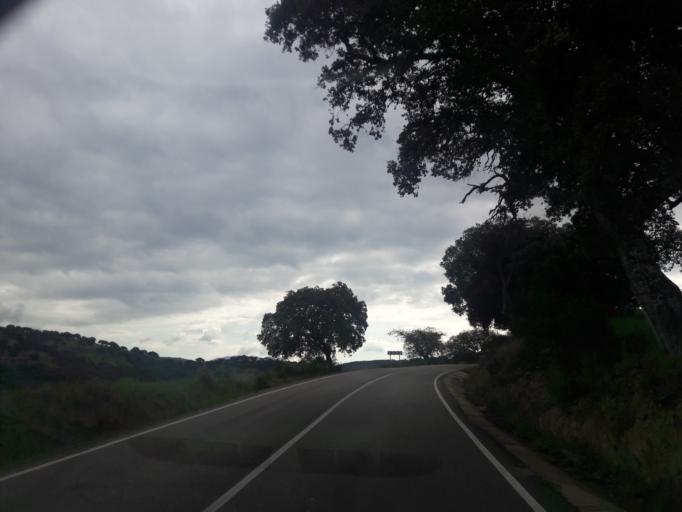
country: ES
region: Castille and Leon
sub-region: Provincia de Salamanca
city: Serradilla del Arroyo
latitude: 40.5203
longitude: -6.4011
